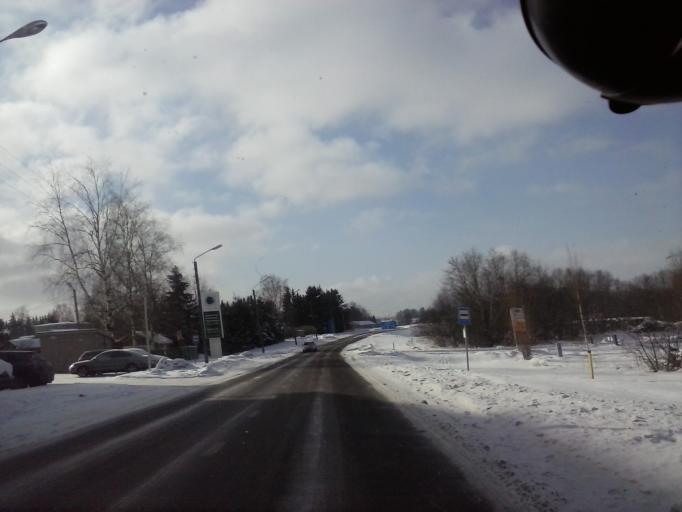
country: EE
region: Viljandimaa
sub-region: Viljandi linn
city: Viljandi
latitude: 58.3571
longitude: 25.5644
